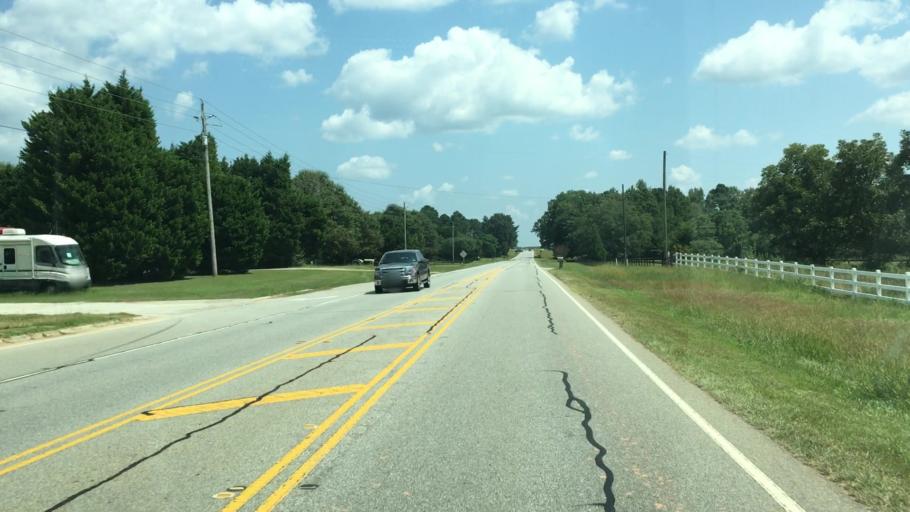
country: US
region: Georgia
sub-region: Oconee County
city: Bogart
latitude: 33.8798
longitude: -83.5442
